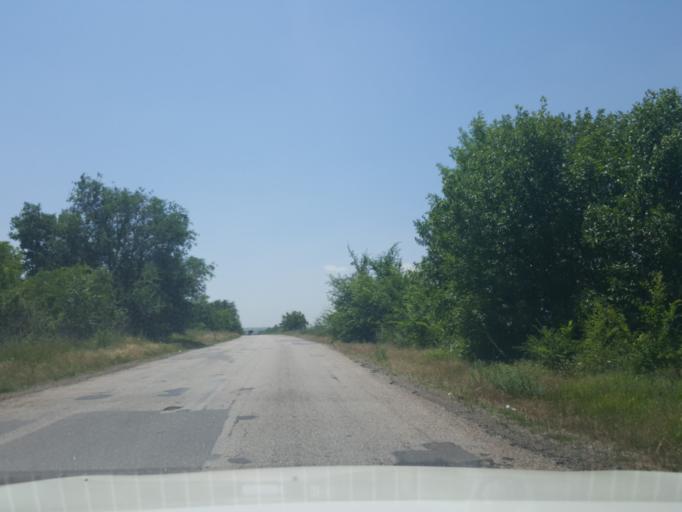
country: UA
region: Odessa
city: Starokozache
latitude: 46.3902
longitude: 30.0900
